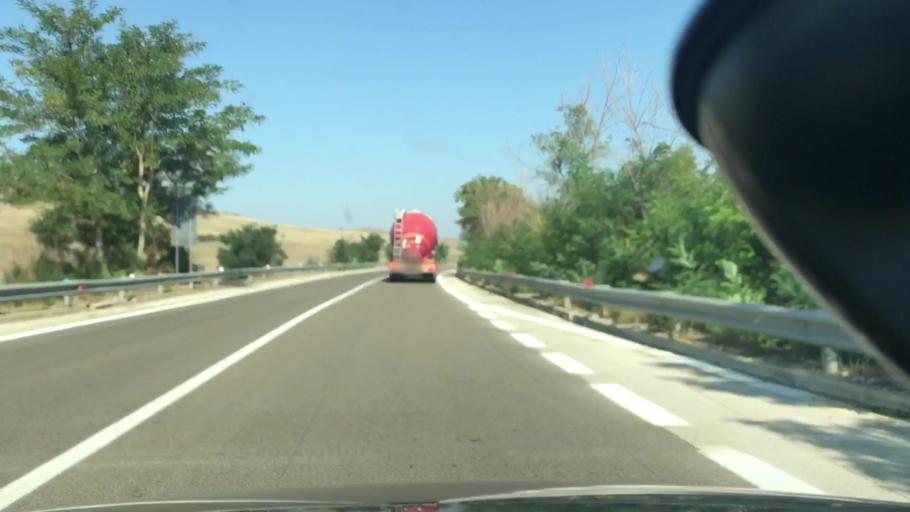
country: IT
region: Basilicate
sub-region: Provincia di Matera
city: Irsina
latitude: 40.7936
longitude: 16.2787
